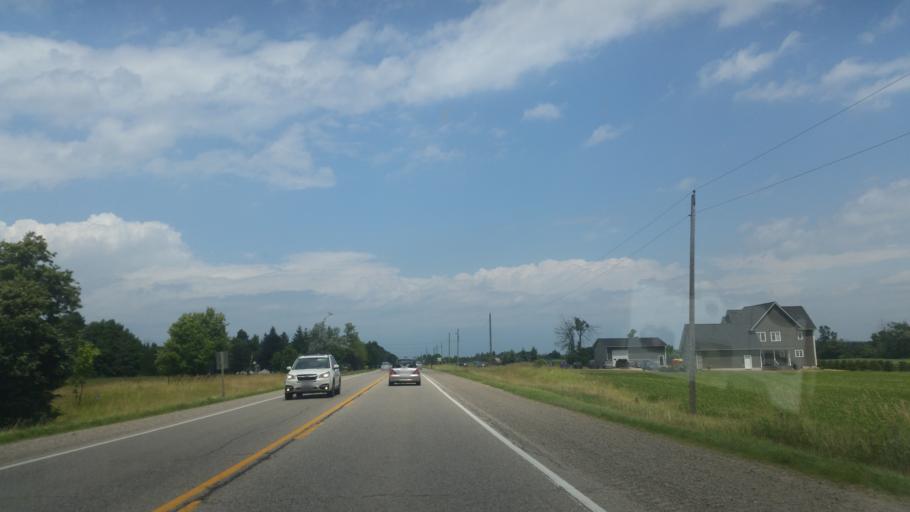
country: CA
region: Ontario
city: Orangeville
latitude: 43.7388
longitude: -80.0842
